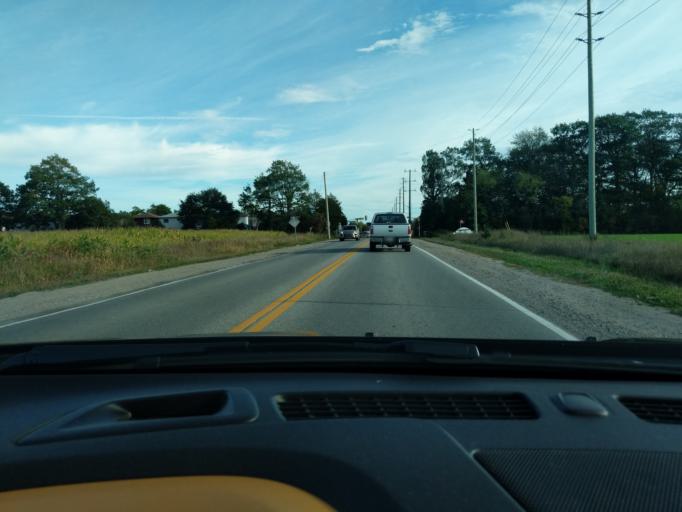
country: CA
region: Ontario
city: Barrie
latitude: 44.3975
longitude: -79.7388
